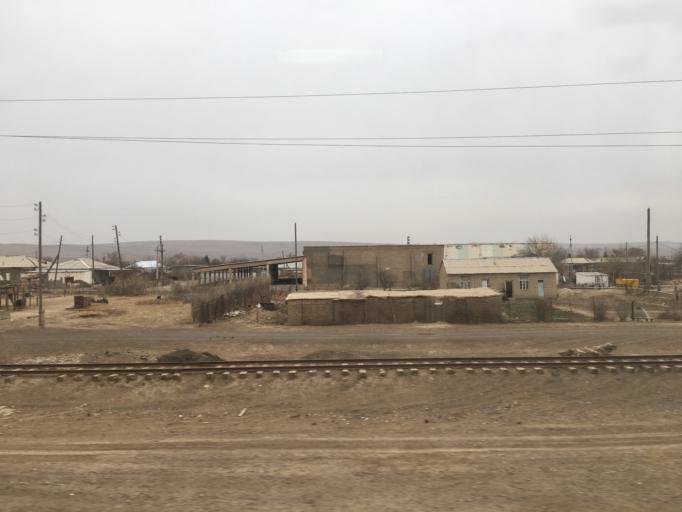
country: TM
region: Mary
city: Yoloeten
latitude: 36.5453
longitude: 62.5537
